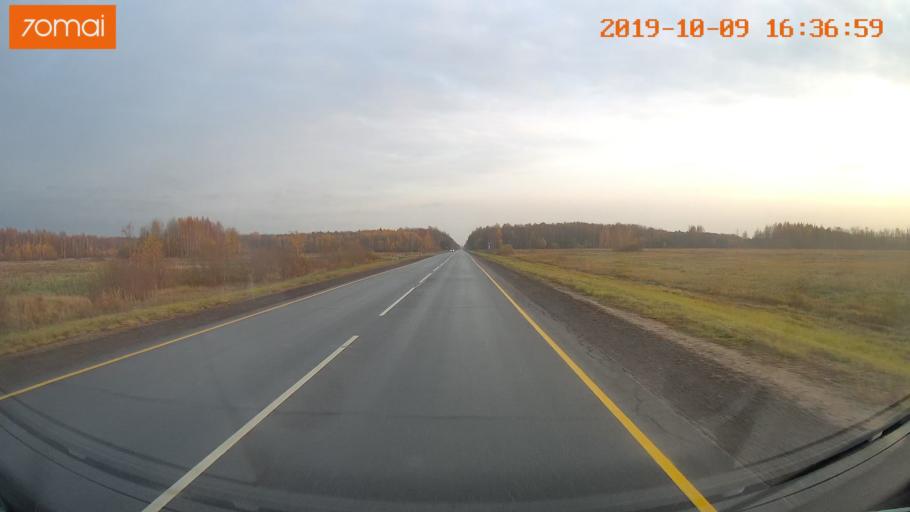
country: RU
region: Kostroma
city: Volgorechensk
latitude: 57.5337
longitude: 41.0191
